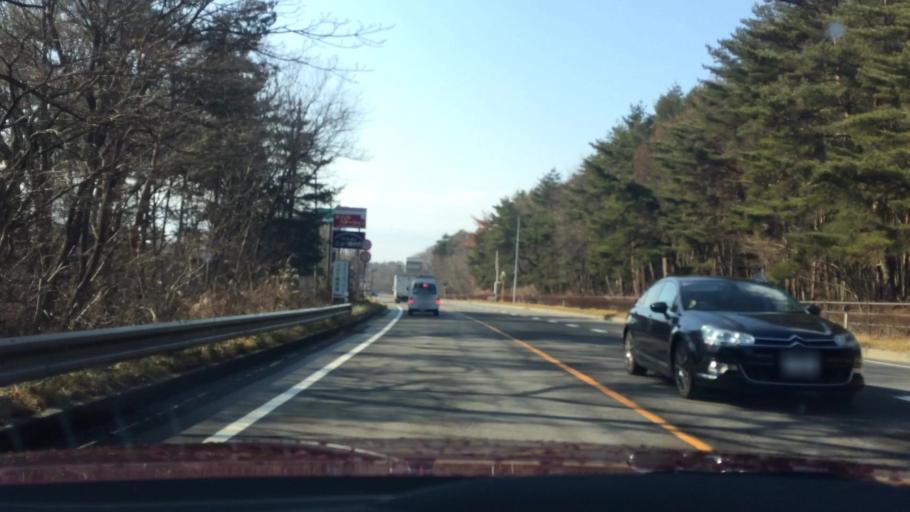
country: JP
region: Nagano
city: Komoro
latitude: 36.3328
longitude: 138.5245
